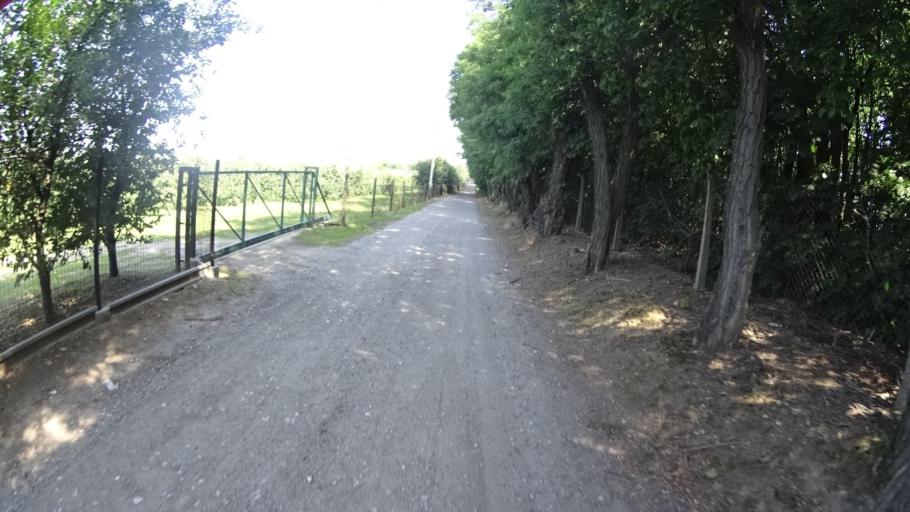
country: PL
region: Masovian Voivodeship
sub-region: Powiat grojecki
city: Grojec
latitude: 51.8476
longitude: 20.8575
